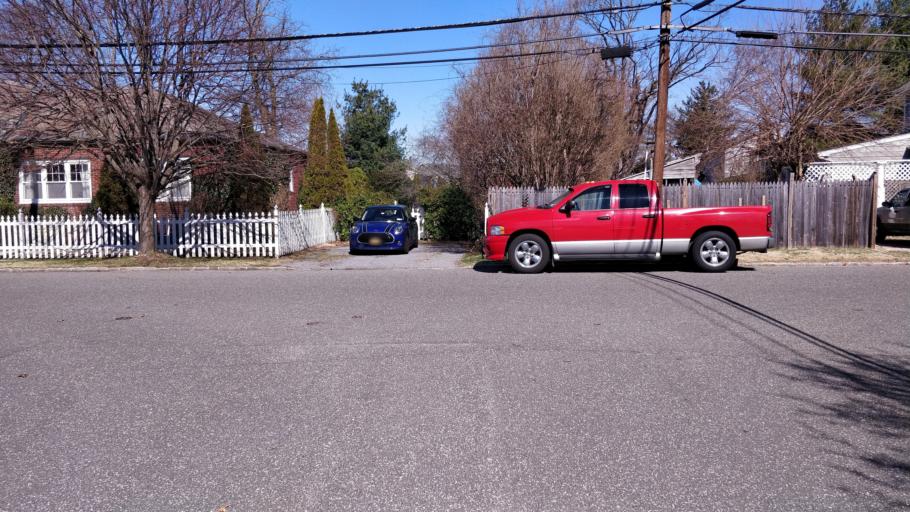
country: US
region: New York
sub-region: Nassau County
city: East Norwich
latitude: 40.8468
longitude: -73.5335
